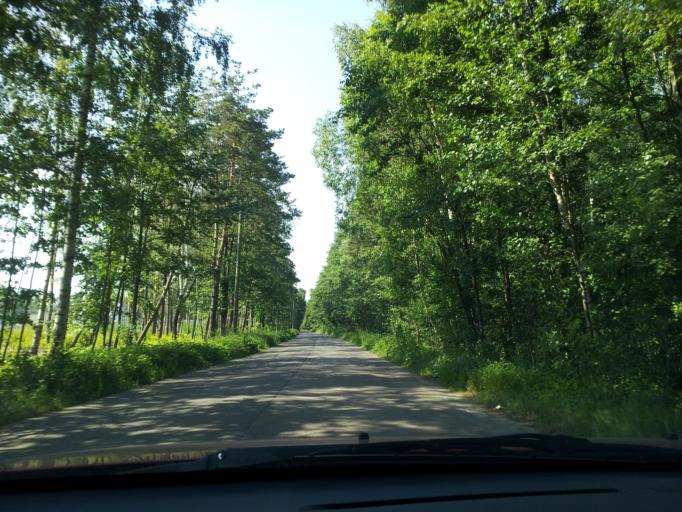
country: LV
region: Riga
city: Bolderaja
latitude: 57.0582
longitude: 24.0587
